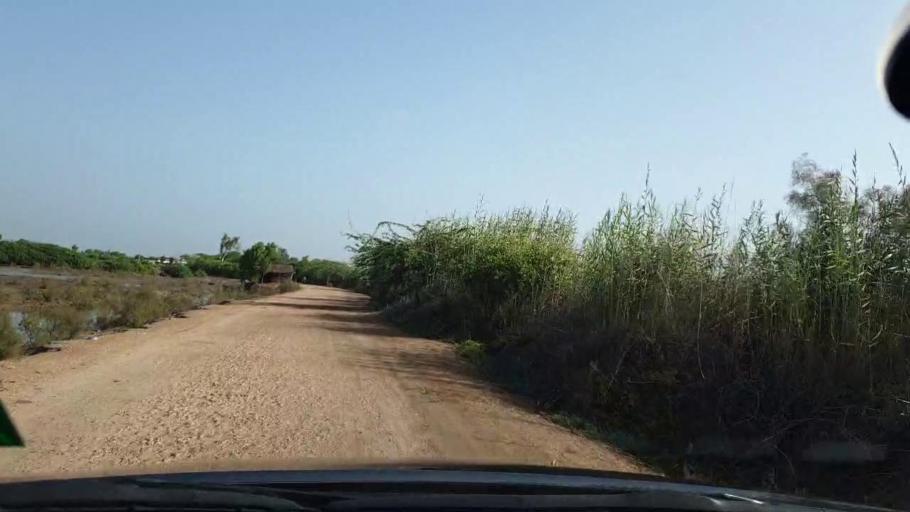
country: PK
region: Sindh
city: Tando Bago
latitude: 24.6573
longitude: 69.0419
